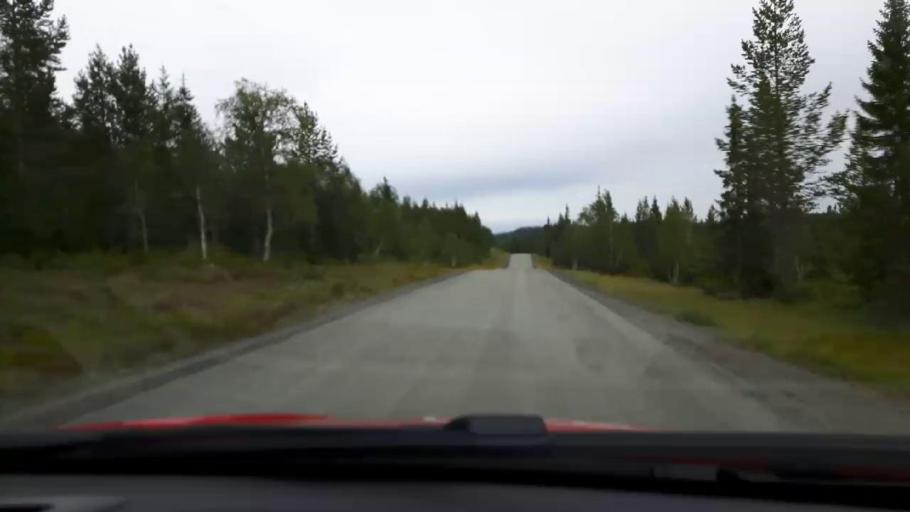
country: SE
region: Jaemtland
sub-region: Are Kommun
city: Are
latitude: 63.4363
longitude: 13.2651
